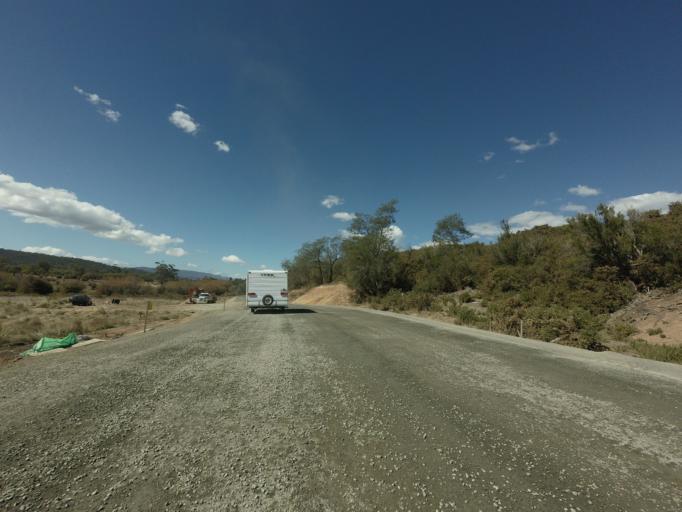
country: AU
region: Tasmania
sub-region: Break O'Day
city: St Helens
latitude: -41.6514
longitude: 147.9278
